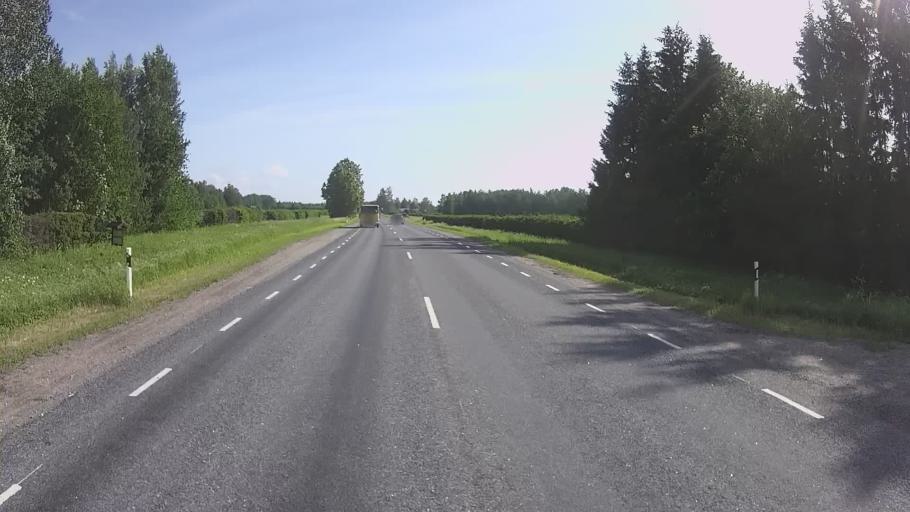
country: EE
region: Valgamaa
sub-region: Torva linn
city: Torva
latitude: 58.0110
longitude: 25.9395
